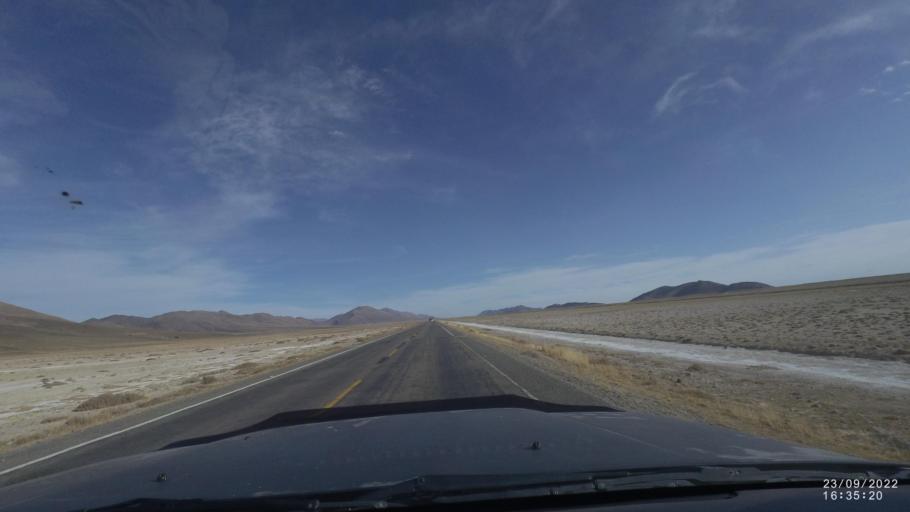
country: BO
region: Oruro
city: Machacamarca
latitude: -18.2030
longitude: -67.0113
